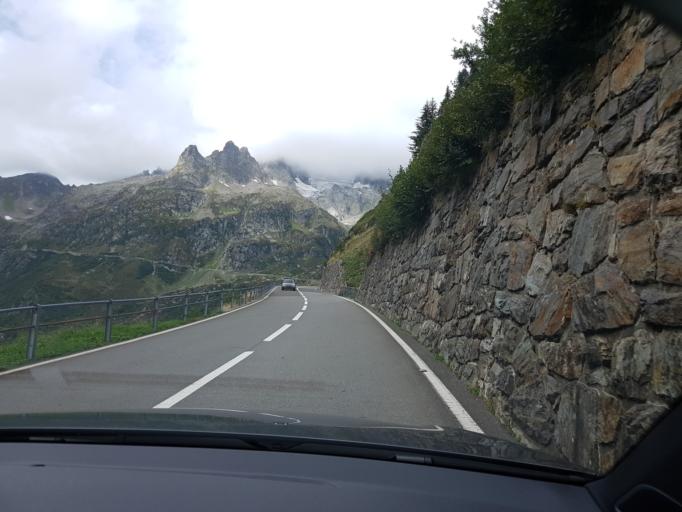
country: CH
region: Obwalden
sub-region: Obwalden
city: Engelberg
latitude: 46.7455
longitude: 8.4854
